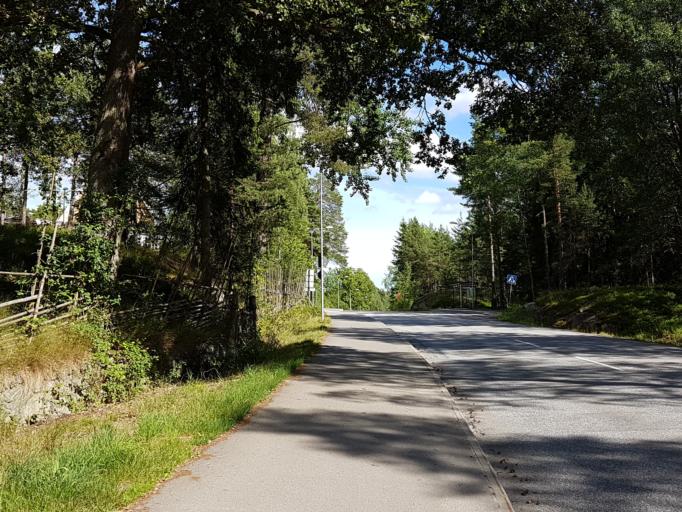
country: SE
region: Stockholm
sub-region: Nacka Kommun
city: Kummelnas
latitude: 59.3437
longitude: 18.2500
